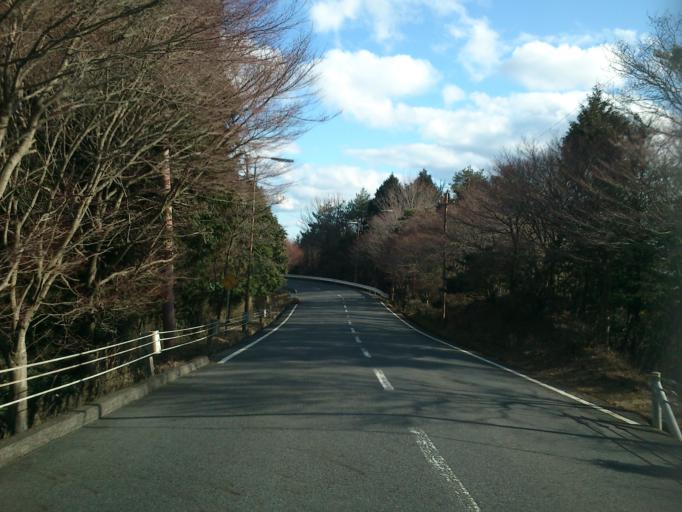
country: JP
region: Shiga Prefecture
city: Otsu-shi
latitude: 35.0526
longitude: 135.8343
